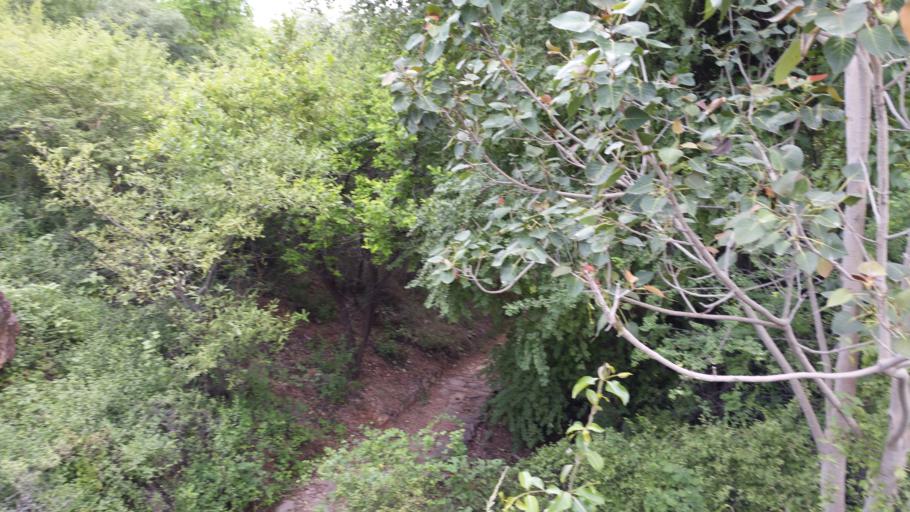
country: IN
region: Rajasthan
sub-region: Jodhpur
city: Jodhpur
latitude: 26.3028
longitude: 73.0214
